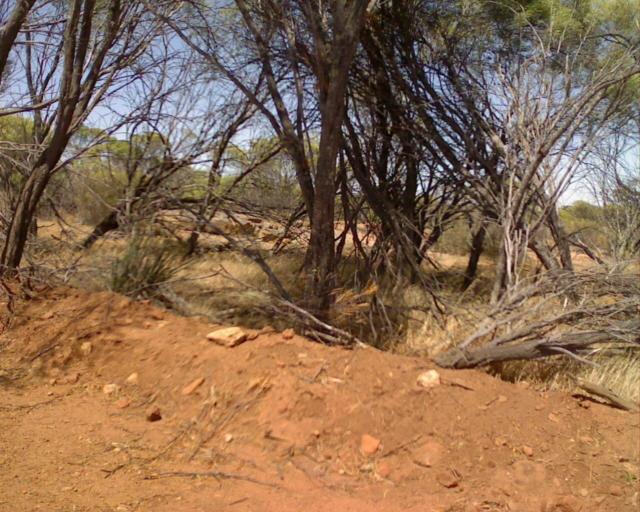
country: AU
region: Western Australia
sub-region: Wongan-Ballidu
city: Wongan Hills
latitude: -30.4257
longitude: 116.9672
